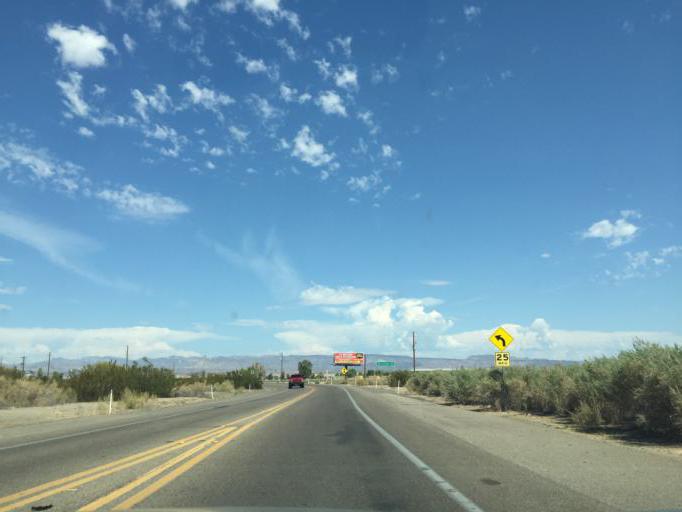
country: US
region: California
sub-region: San Bernardino County
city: Needles
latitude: 34.8638
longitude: -114.5997
